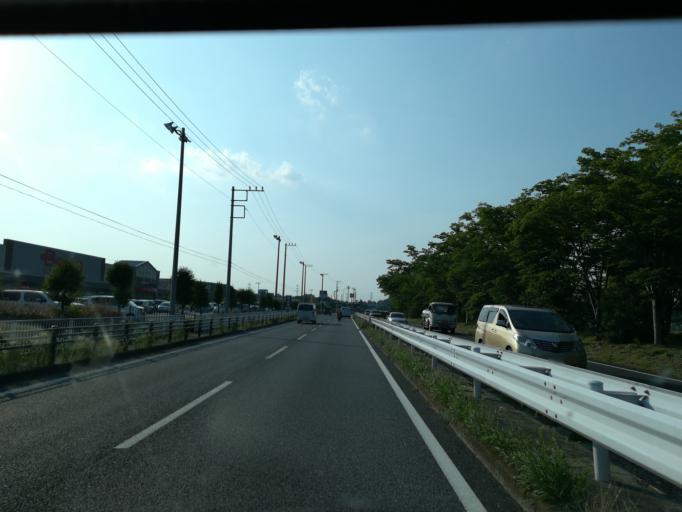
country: JP
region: Saitama
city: Kumagaya
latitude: 36.0590
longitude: 139.3705
